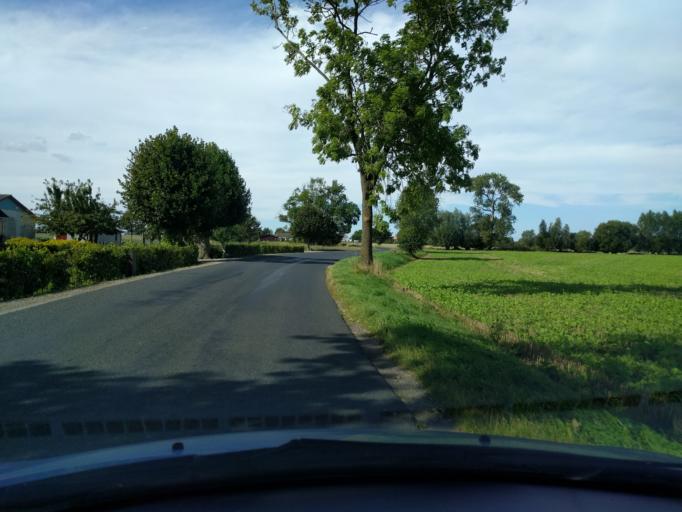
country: DK
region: South Denmark
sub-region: Kerteminde Kommune
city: Kerteminde
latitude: 55.4346
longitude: 10.6081
